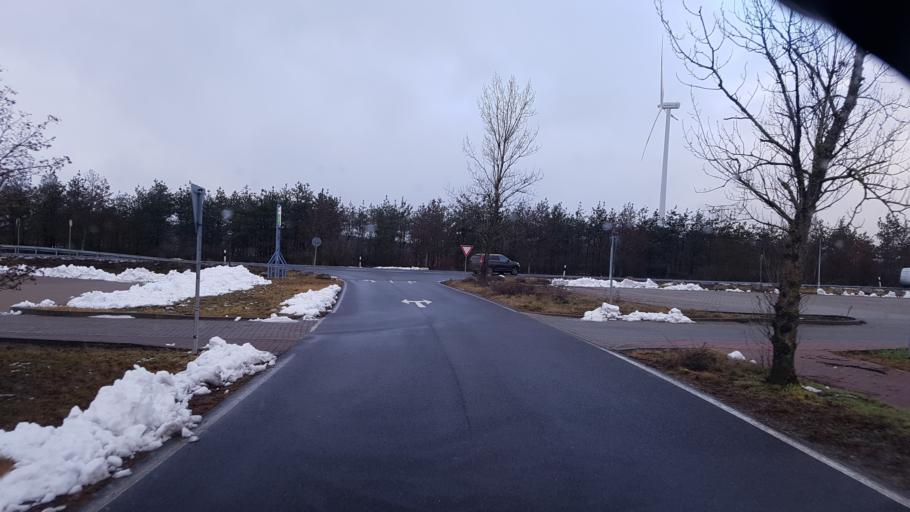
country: DE
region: Brandenburg
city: Heinersbruck
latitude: 51.7908
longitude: 14.4841
